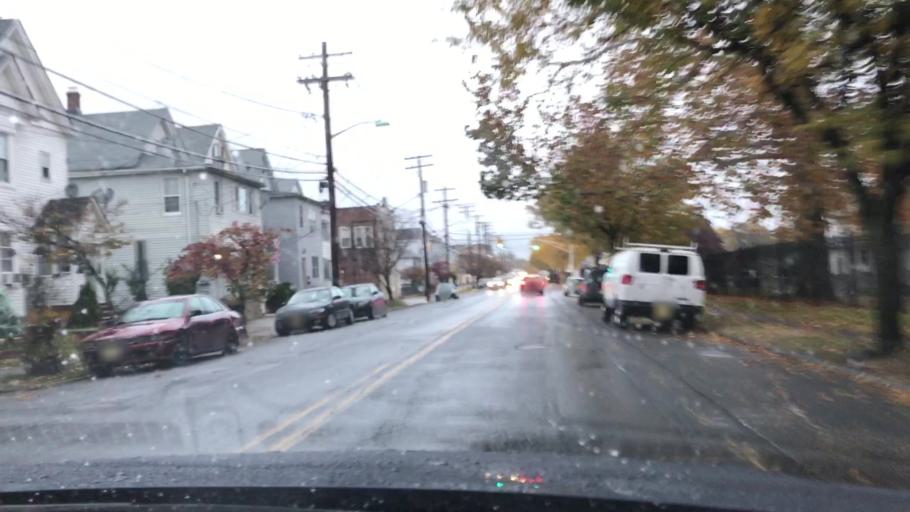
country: US
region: New Jersey
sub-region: Bergen County
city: Lodi
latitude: 40.8710
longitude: -74.0950
